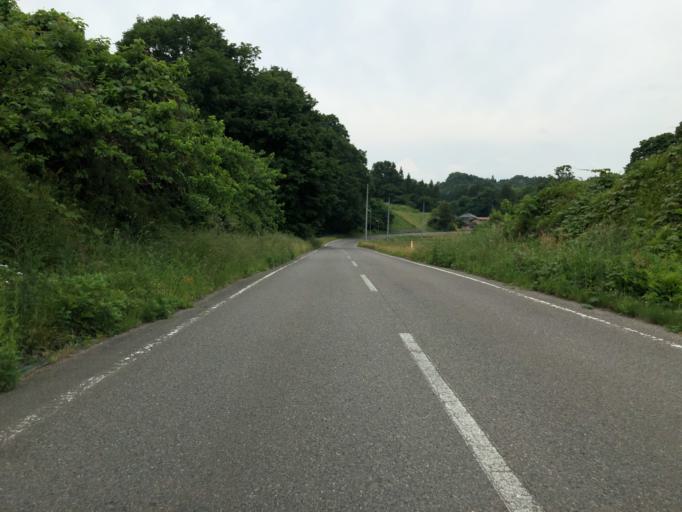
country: JP
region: Fukushima
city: Miharu
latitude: 37.4655
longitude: 140.5260
